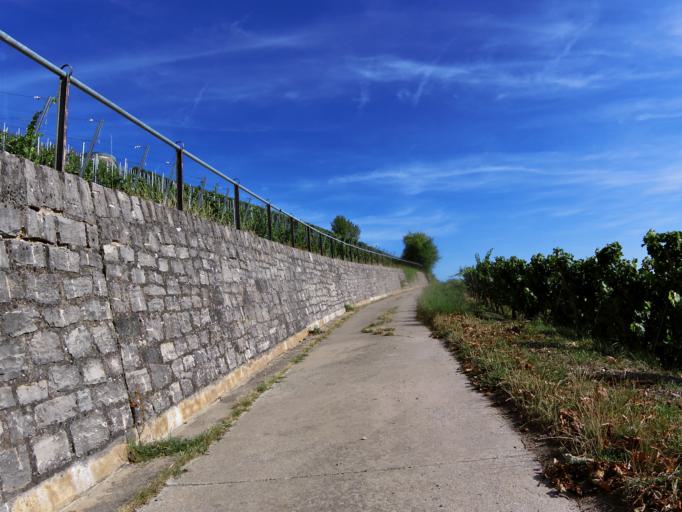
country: DE
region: Bavaria
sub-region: Regierungsbezirk Unterfranken
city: Randersacker
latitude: 49.7510
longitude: 9.9911
